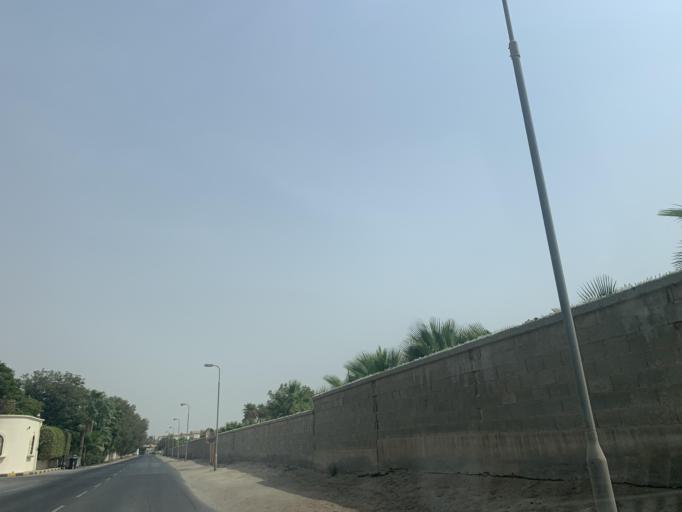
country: BH
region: Manama
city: Jidd Hafs
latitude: 26.2040
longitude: 50.4717
